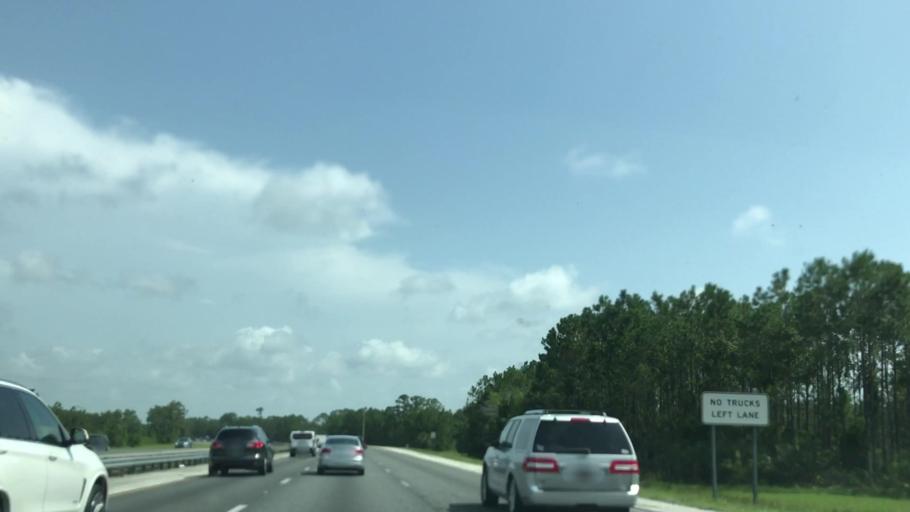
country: US
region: Florida
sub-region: Volusia County
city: Ormond-by-the-Sea
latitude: 29.3445
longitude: -81.1308
